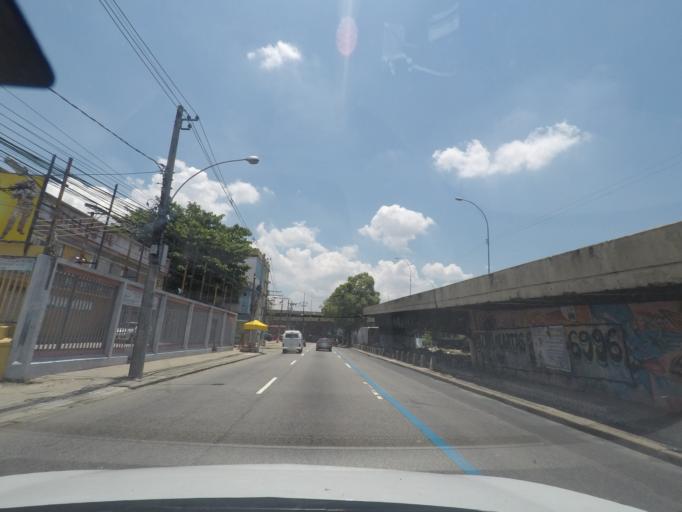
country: BR
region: Rio de Janeiro
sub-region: Rio De Janeiro
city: Rio de Janeiro
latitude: -22.9024
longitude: -43.2591
